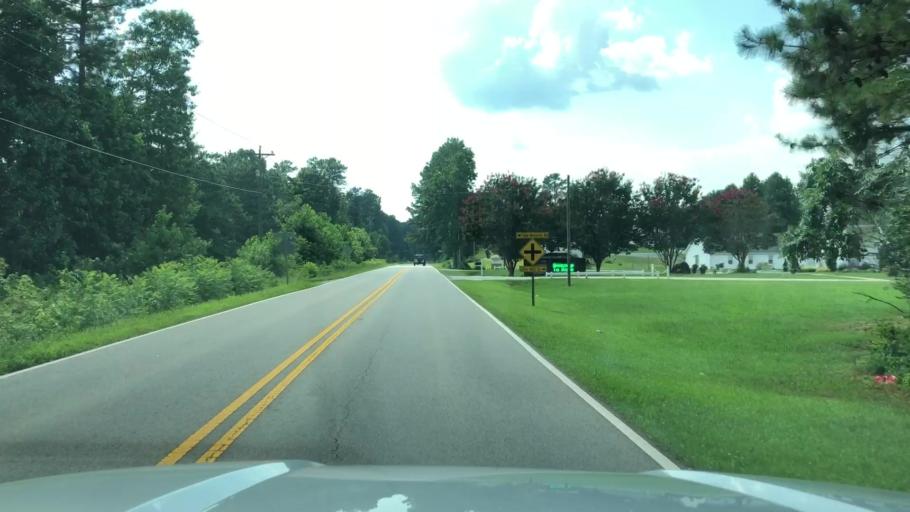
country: US
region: Georgia
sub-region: Paulding County
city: Hiram
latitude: 33.9380
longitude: -84.7569
